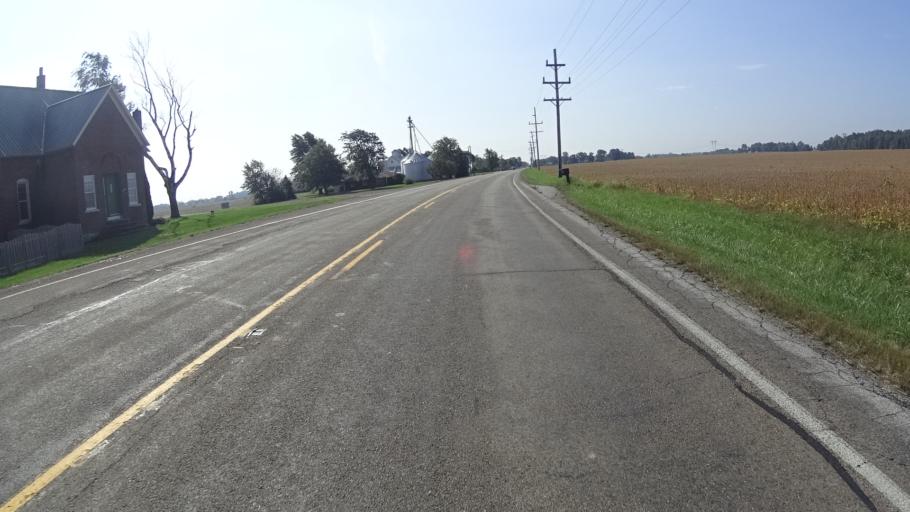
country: US
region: Indiana
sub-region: Madison County
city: Lapel
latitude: 40.0448
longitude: -85.8435
